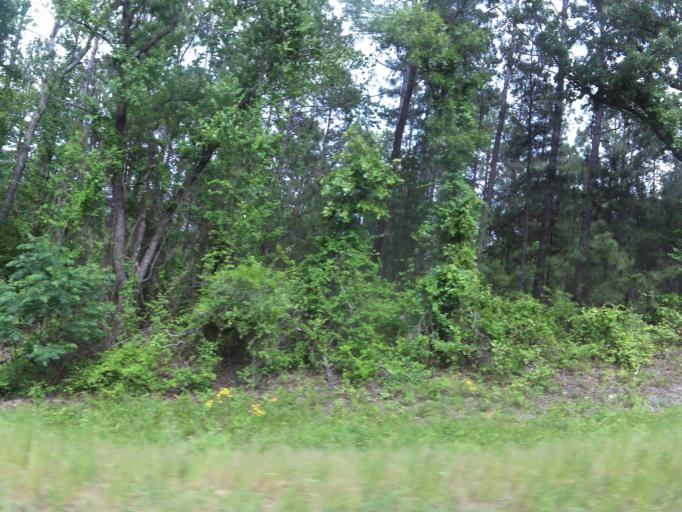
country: US
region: Georgia
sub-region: Jefferson County
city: Wrens
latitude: 33.3251
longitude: -82.4529
